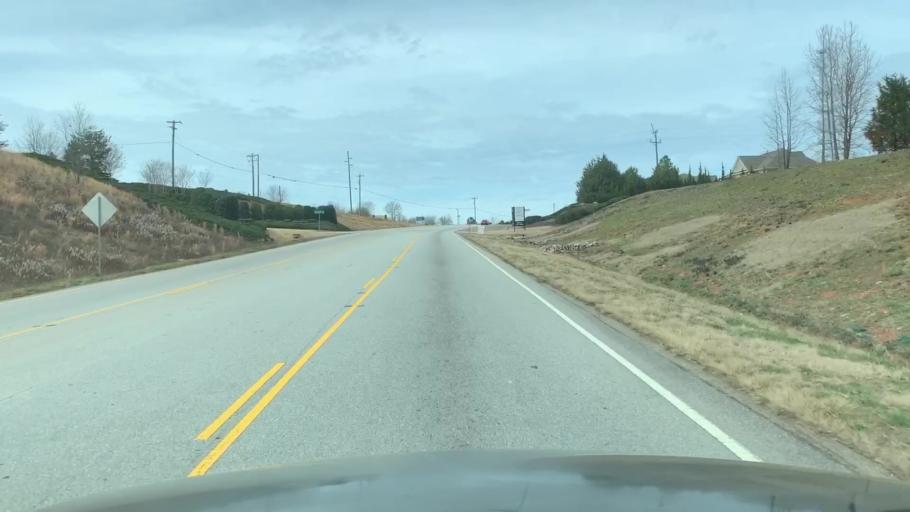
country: US
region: South Carolina
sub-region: Greenville County
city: Golden Grove
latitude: 34.7661
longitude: -82.4565
